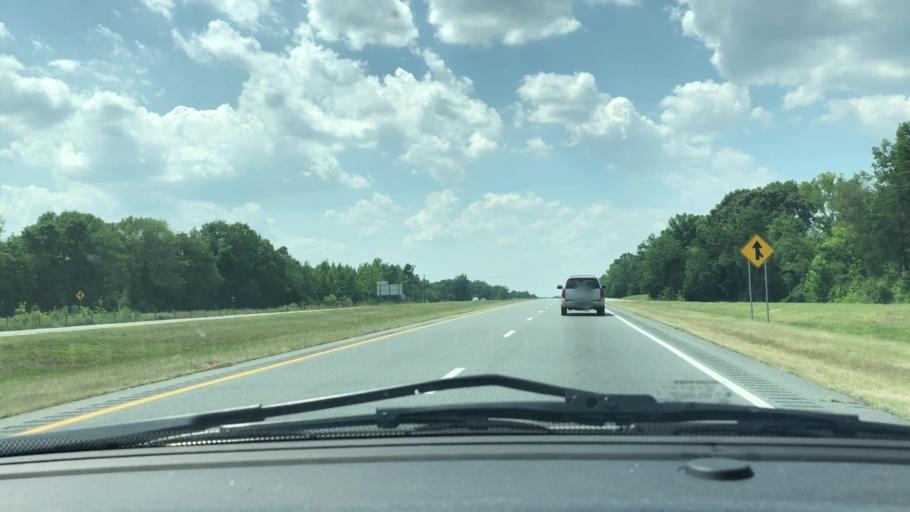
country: US
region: North Carolina
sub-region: Guilford County
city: Forest Oaks
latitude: 35.9654
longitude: -79.7073
